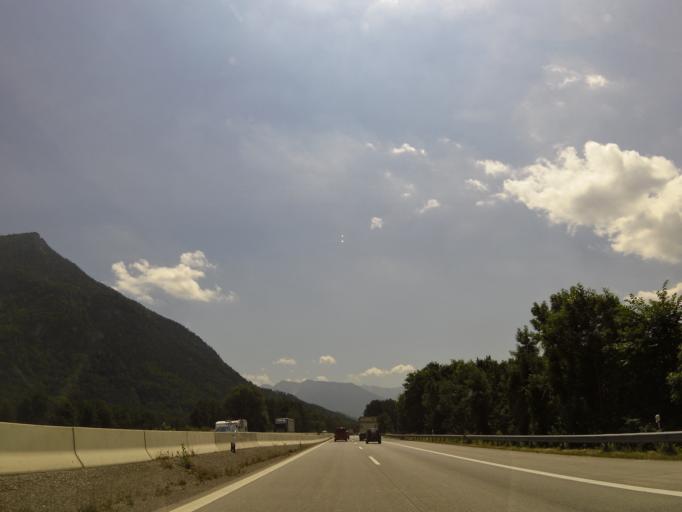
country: DE
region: Bavaria
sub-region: Upper Bavaria
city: Nussdorf am Inn
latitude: 47.7084
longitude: 12.1536
